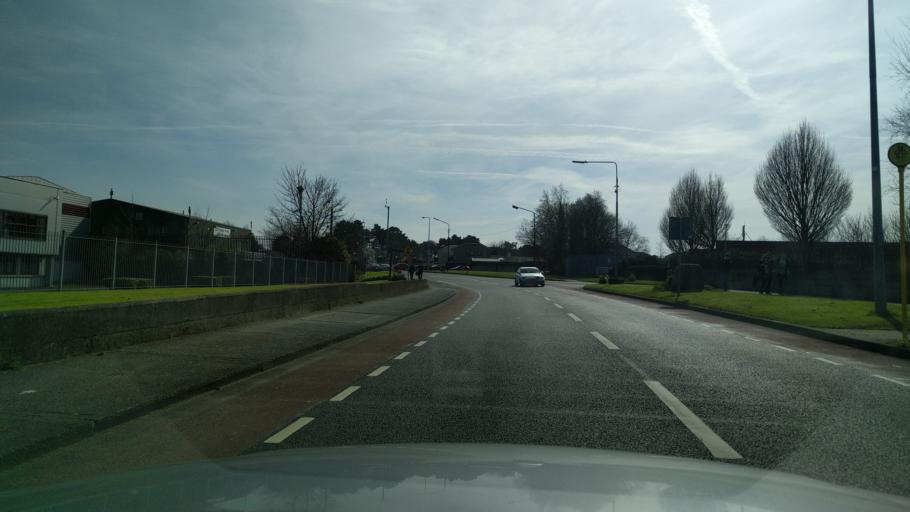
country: IE
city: Palmerstown
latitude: 53.3469
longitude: -6.3795
